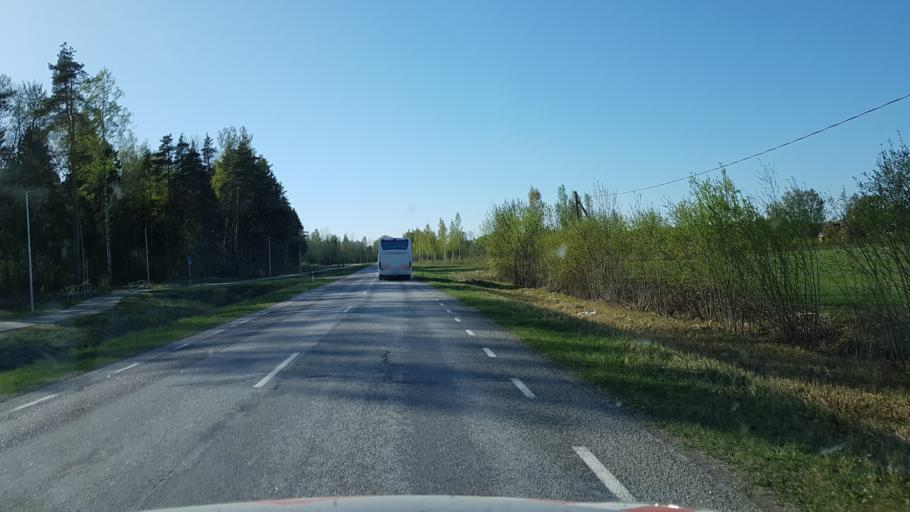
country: EE
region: Paernumaa
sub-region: Paikuse vald
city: Paikuse
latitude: 58.3642
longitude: 24.6458
